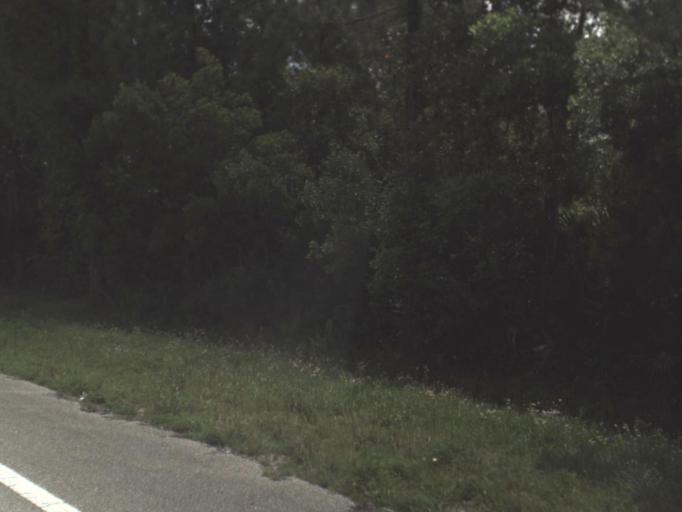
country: US
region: Florida
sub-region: Saint Johns County
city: Saint Augustine Shores
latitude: 29.7460
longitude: -81.3513
